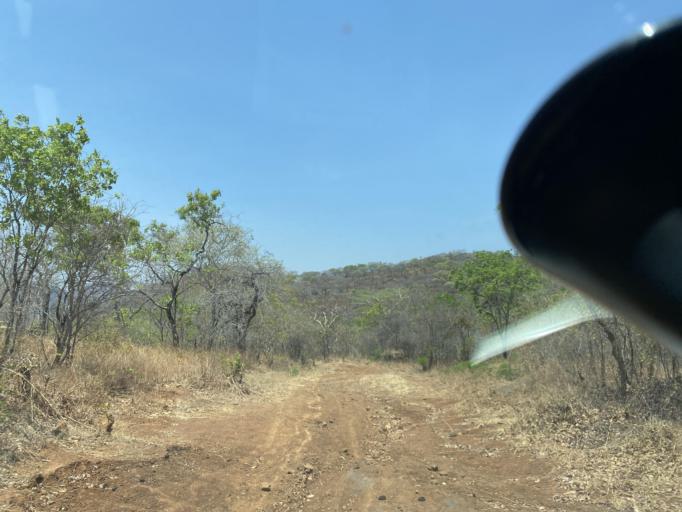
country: ZM
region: Lusaka
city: Kafue
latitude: -15.8007
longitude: 28.4542
